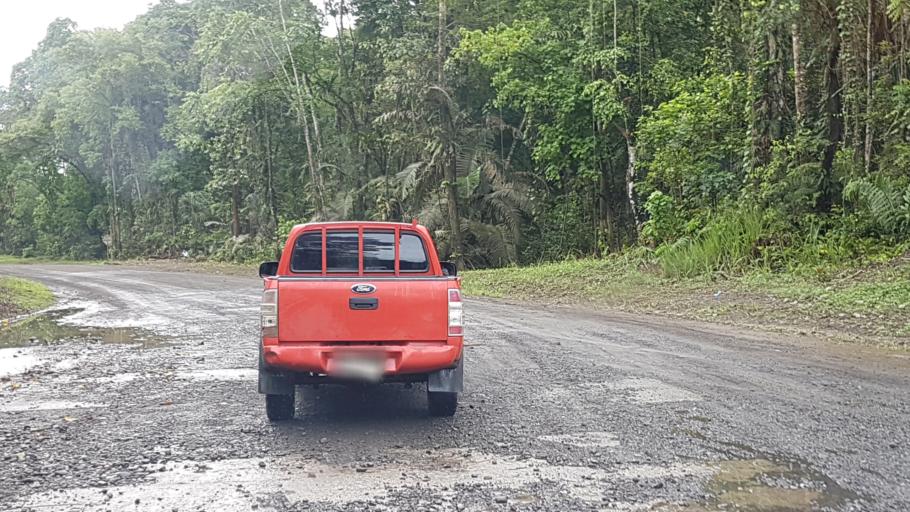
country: PG
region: Milne Bay
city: Alotau
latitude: -10.3325
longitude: 150.5325
